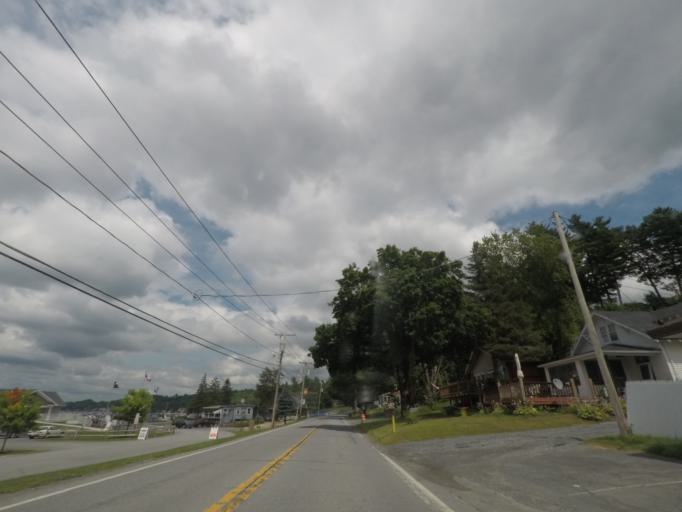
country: US
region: New York
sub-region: Saratoga County
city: Country Knolls
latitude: 42.9853
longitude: -73.7439
